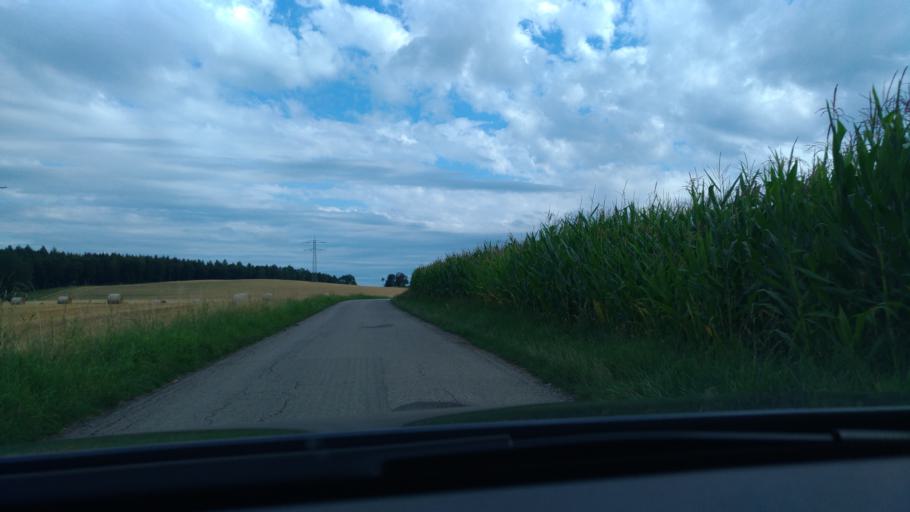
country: DE
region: Baden-Wuerttemberg
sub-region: Tuebingen Region
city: Sipplingen
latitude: 47.8022
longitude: 9.1219
